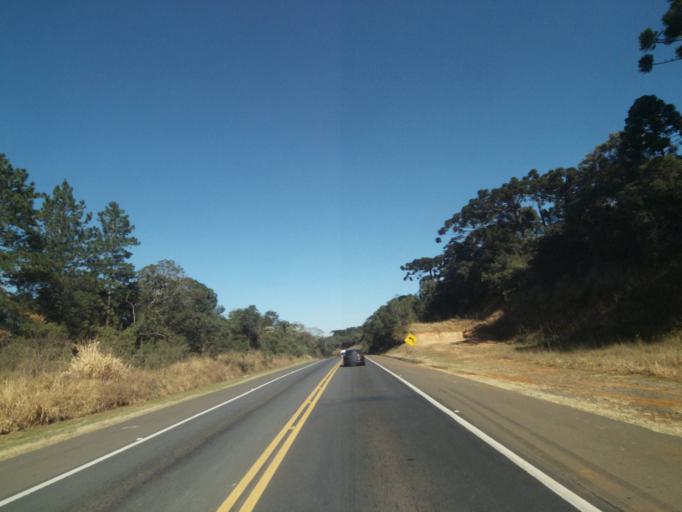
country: BR
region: Parana
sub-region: Tibagi
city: Tibagi
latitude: -24.7272
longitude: -50.5383
